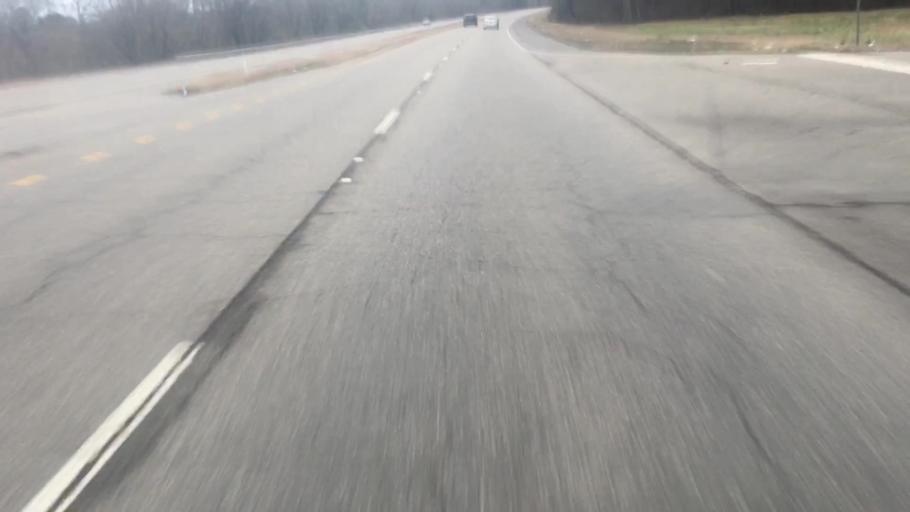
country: US
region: Alabama
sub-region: Walker County
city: Cordova
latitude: 33.8174
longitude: -87.1506
